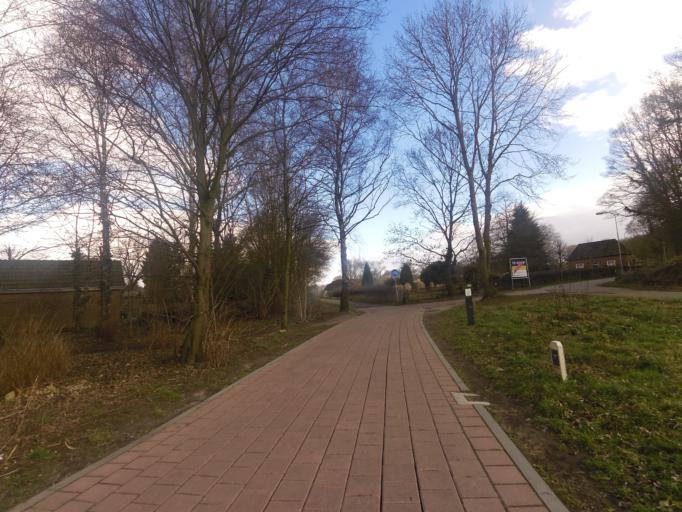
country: NL
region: Gelderland
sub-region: Gemeente Doetinchem
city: Doetinchem
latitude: 51.9589
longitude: 6.3051
